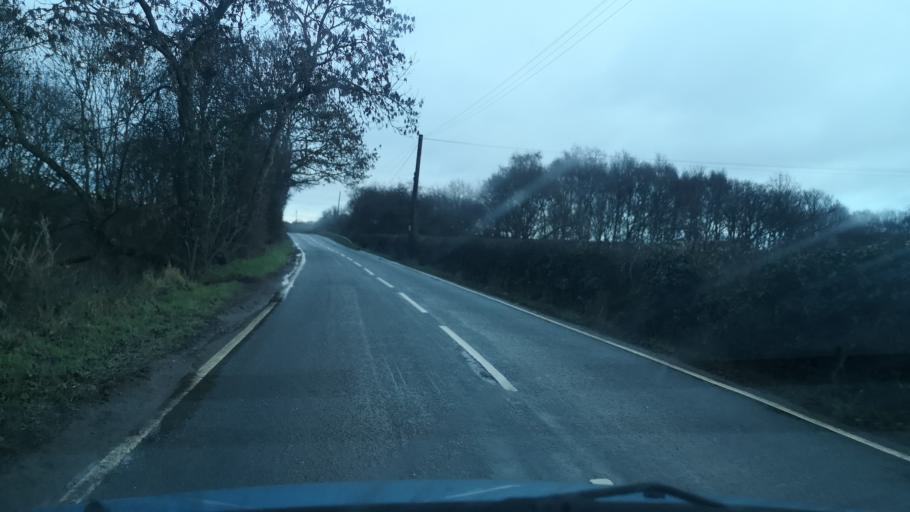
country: GB
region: England
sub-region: City and Borough of Wakefield
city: Fitzwilliam
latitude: 53.6415
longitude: -1.3981
